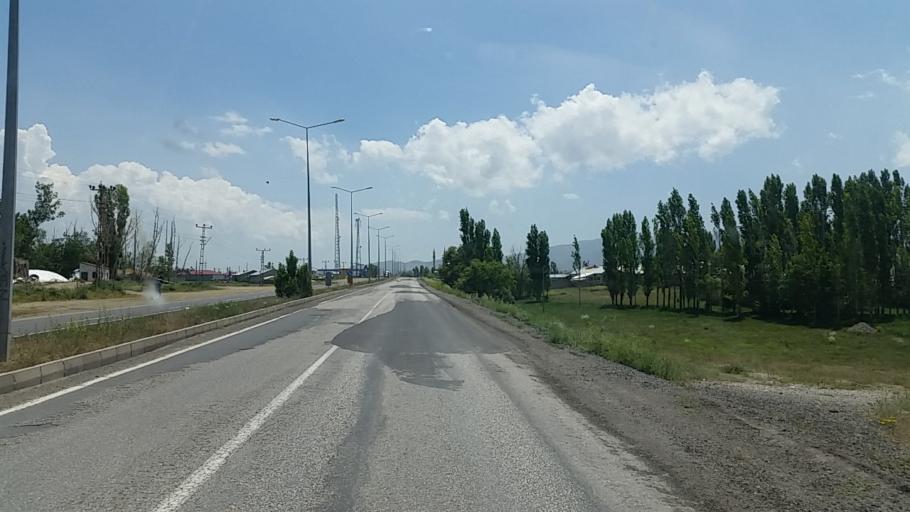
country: TR
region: Agri
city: Taslicay
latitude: 39.6410
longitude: 43.3743
